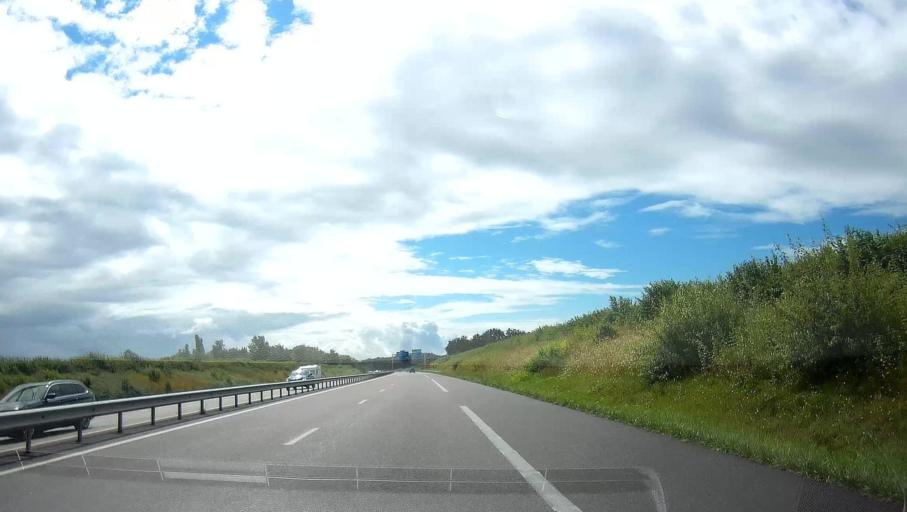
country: FR
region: Champagne-Ardenne
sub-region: Departement de l'Aube
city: Verrieres
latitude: 48.2442
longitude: 4.1697
